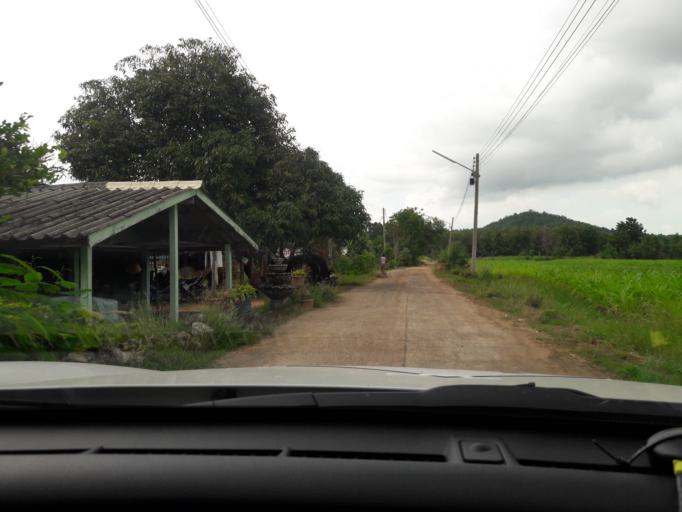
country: TH
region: Nakhon Sawan
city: Tak Fa
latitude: 15.3572
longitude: 100.4950
